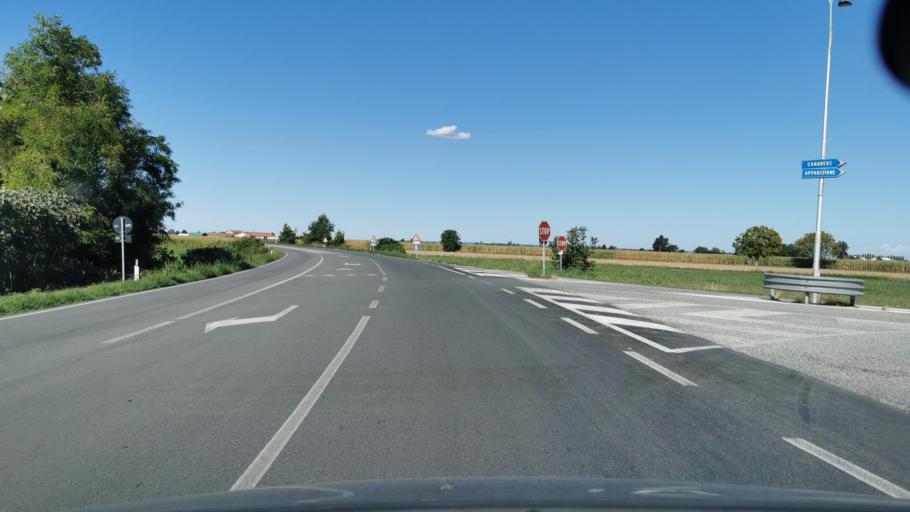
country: IT
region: Piedmont
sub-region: Provincia di Cuneo
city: Savigliano
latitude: 44.6410
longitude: 7.6725
